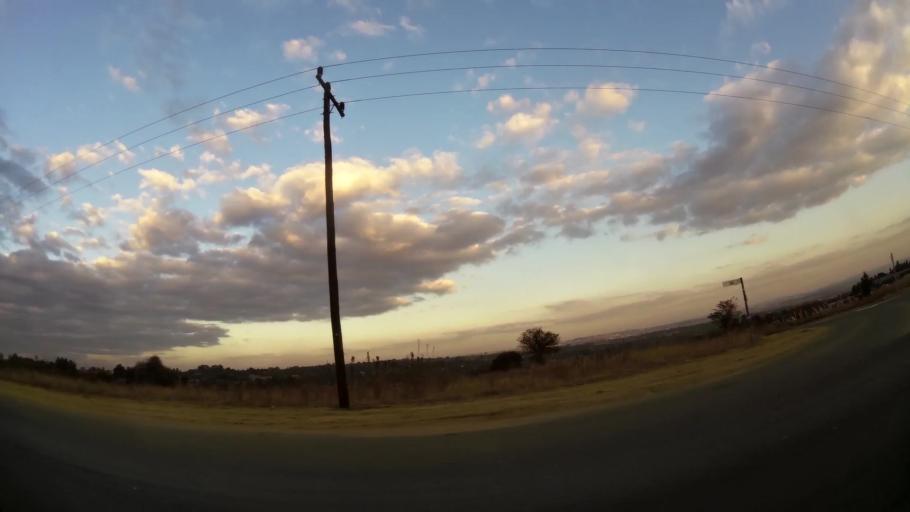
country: ZA
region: Gauteng
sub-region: City of Johannesburg Metropolitan Municipality
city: Midrand
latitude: -25.9972
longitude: 28.1428
